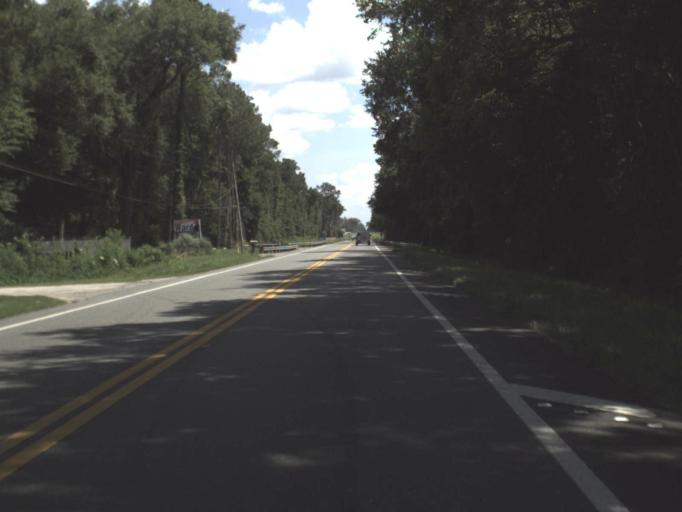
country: US
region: Florida
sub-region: Columbia County
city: Watertown
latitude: 30.0923
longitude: -82.6022
